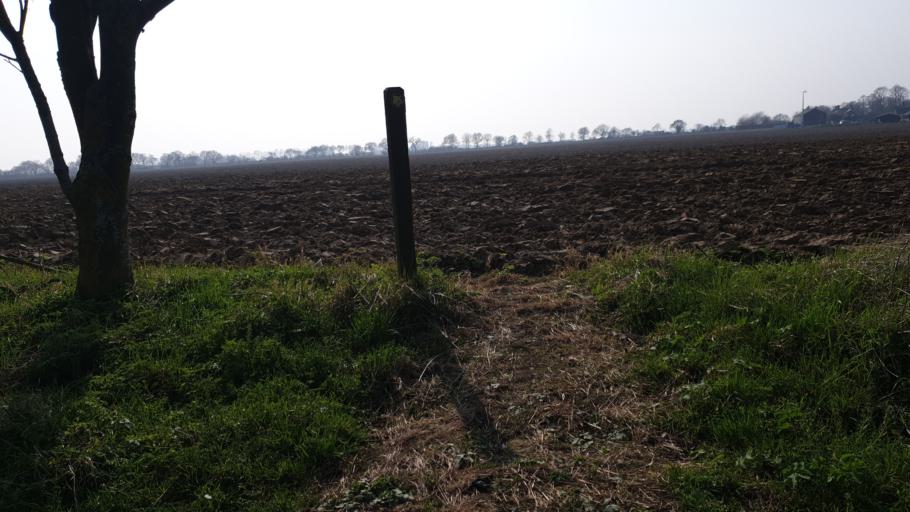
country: GB
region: England
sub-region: Essex
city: Mistley
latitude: 51.9072
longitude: 1.1272
